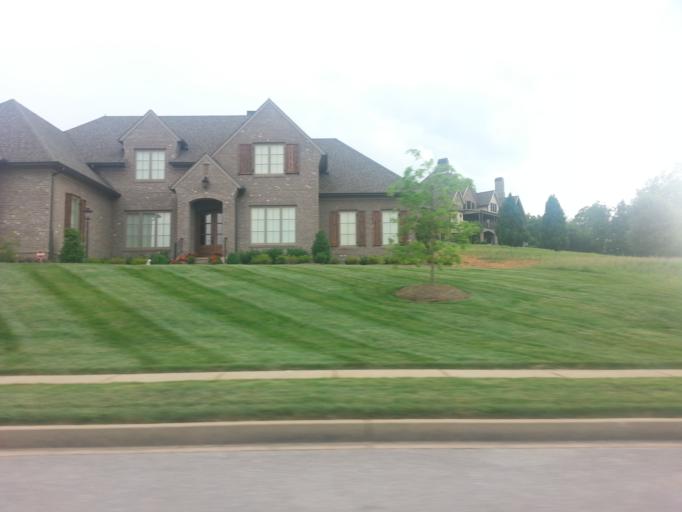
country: US
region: Tennessee
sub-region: Knox County
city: Farragut
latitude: 35.8526
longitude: -84.1946
